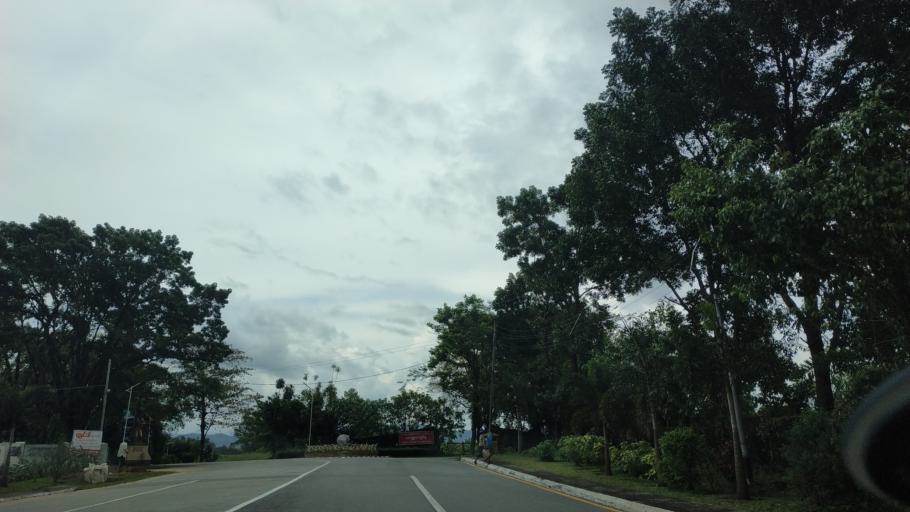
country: MM
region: Tanintharyi
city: Dawei
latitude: 14.0872
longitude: 98.2080
